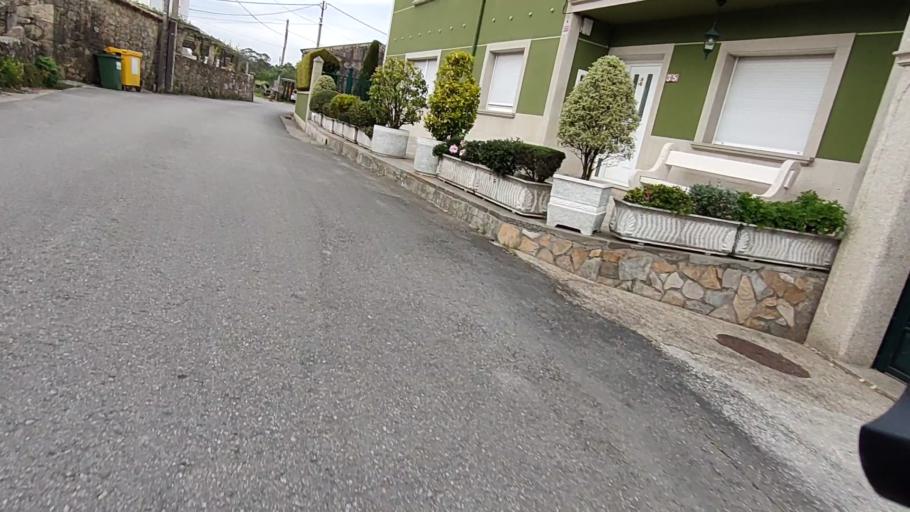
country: ES
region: Galicia
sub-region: Provincia da Coruna
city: Boiro
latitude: 42.6334
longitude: -8.8636
